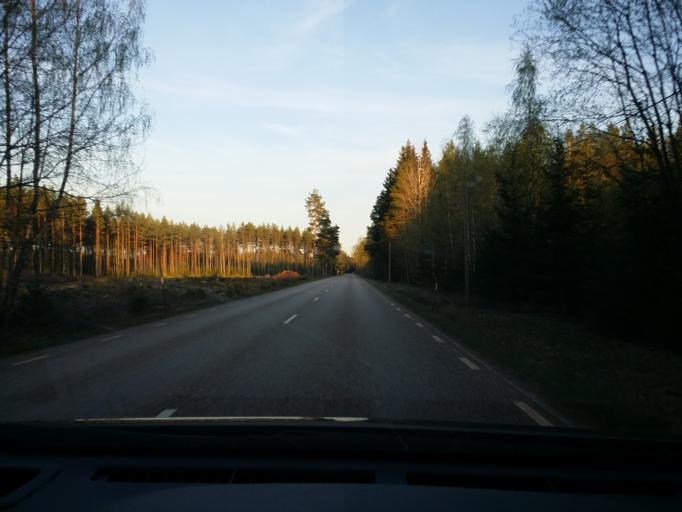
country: SE
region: Vaestmanland
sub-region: Sala Kommun
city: Sala
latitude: 59.8302
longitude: 16.5134
